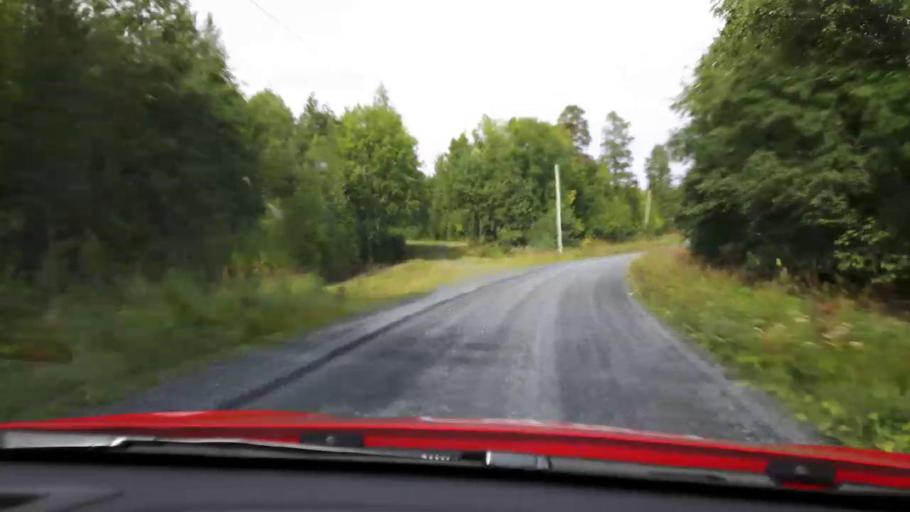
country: SE
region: Jaemtland
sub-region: Are Kommun
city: Jarpen
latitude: 63.2781
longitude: 13.7334
